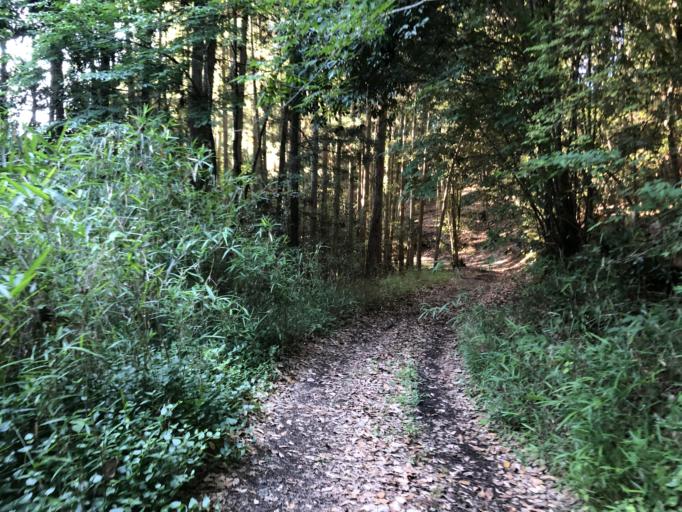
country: JP
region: Kyoto
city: Kameoka
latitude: 34.9884
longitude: 135.6225
